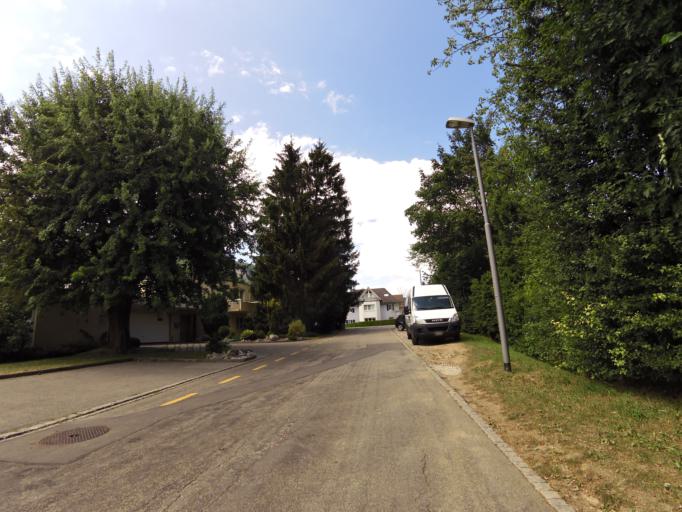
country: CH
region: Solothurn
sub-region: Bezirk Gaeu
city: Oensingen
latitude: 47.2881
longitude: 7.7136
